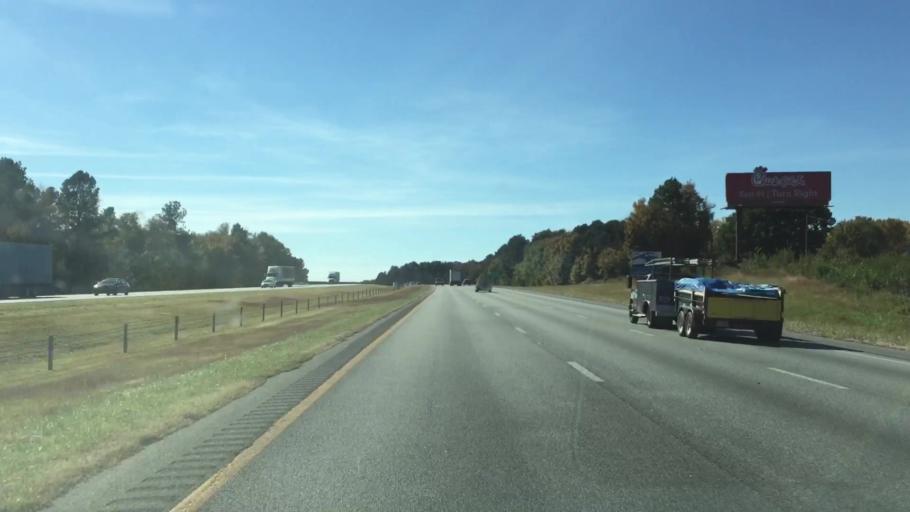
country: US
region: North Carolina
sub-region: Davidson County
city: Lexington
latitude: 35.7985
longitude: -80.2091
